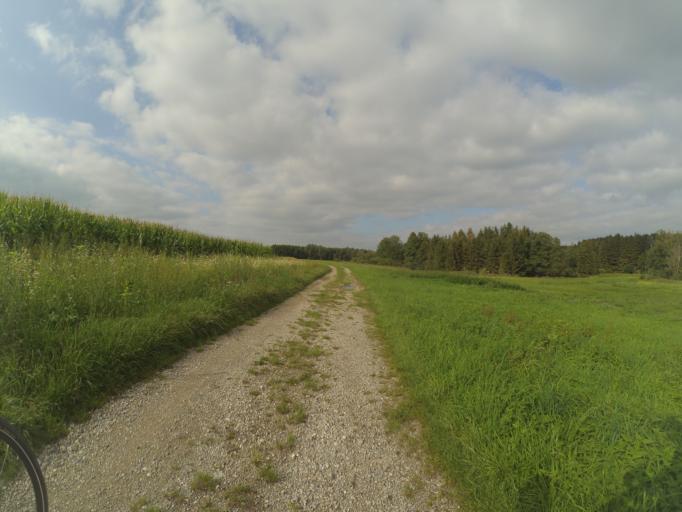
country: DE
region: Bavaria
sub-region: Swabia
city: Lamerdingen
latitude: 48.0566
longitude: 10.7878
